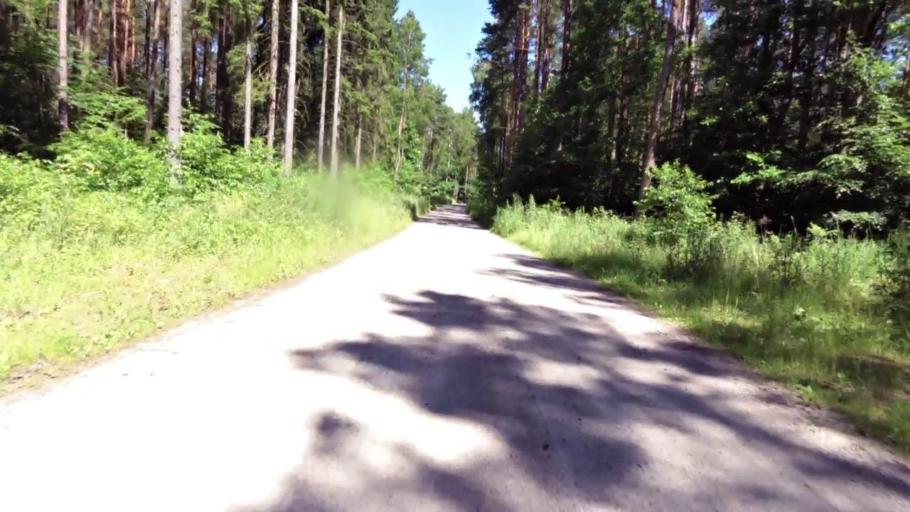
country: PL
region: West Pomeranian Voivodeship
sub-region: Powiat swidwinski
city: Rabino
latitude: 53.8857
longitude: 16.0481
